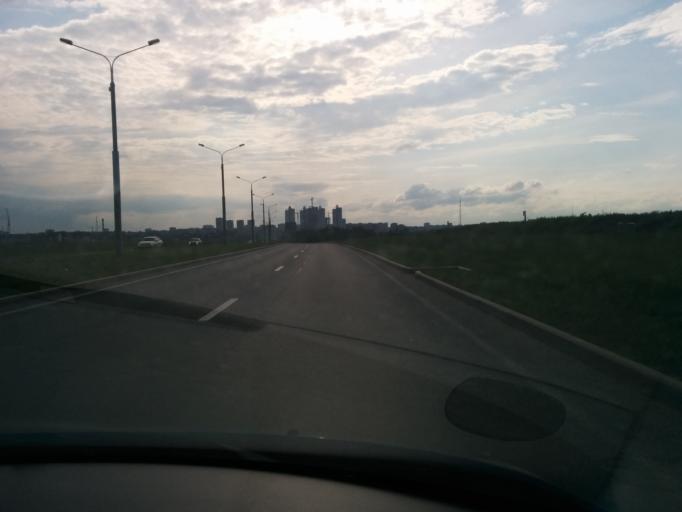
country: RU
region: Perm
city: Perm
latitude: 58.0066
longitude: 56.3525
